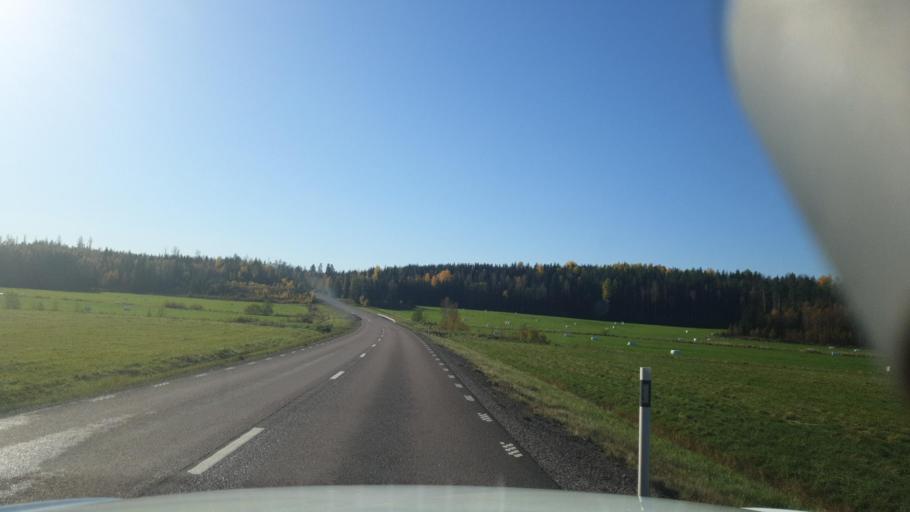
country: SE
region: Vaermland
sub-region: Arvika Kommun
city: Arvika
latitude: 59.4971
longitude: 12.7634
